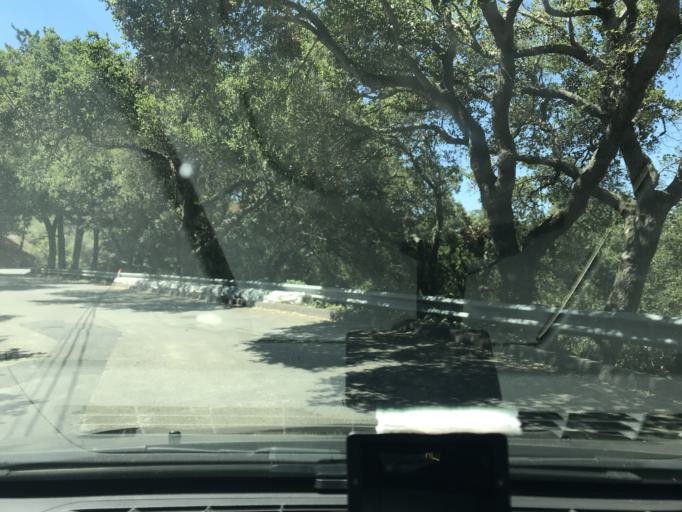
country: US
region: California
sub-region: Santa Clara County
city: Monte Sereno
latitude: 37.2306
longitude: -121.9991
